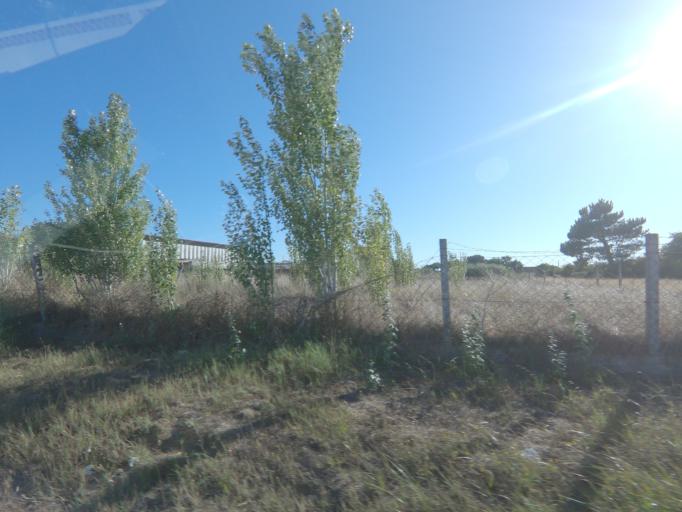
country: PT
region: Setubal
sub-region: Palmela
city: Pinhal Novo
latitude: 38.6098
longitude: -8.9453
